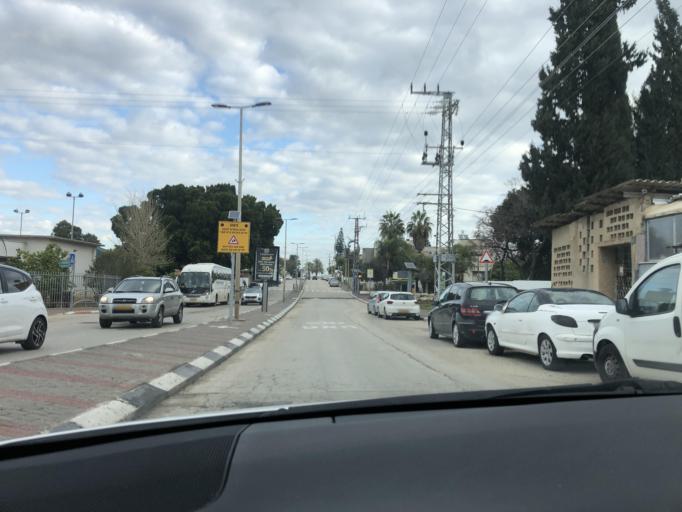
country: IL
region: Central District
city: Rosh Ha'Ayin
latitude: 32.0898
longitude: 34.9539
